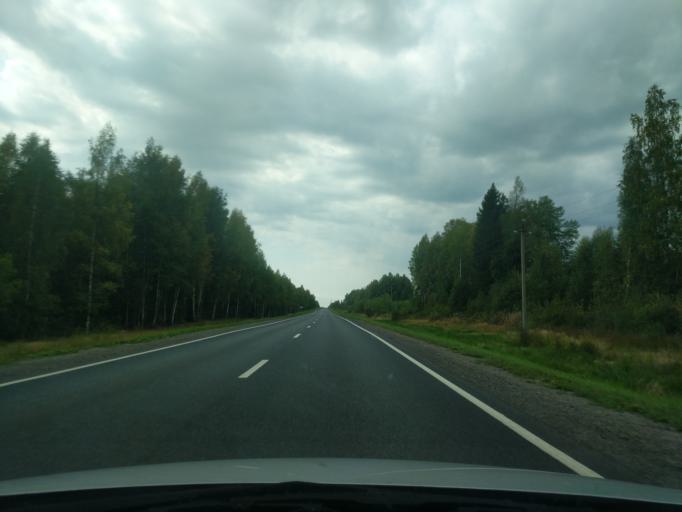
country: RU
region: Kostroma
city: Manturovo
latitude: 58.1536
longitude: 44.3789
